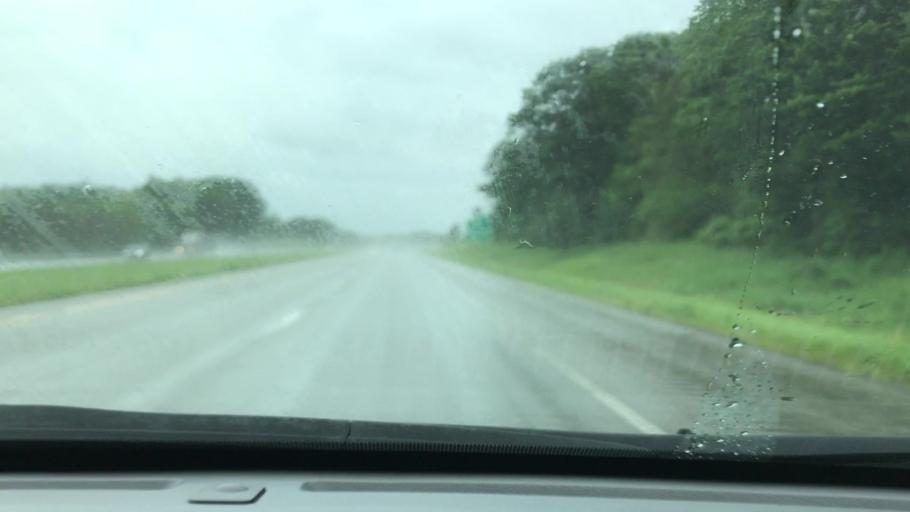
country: US
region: Pennsylvania
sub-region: Blair County
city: Tyrone
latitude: 40.6872
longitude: -78.2257
